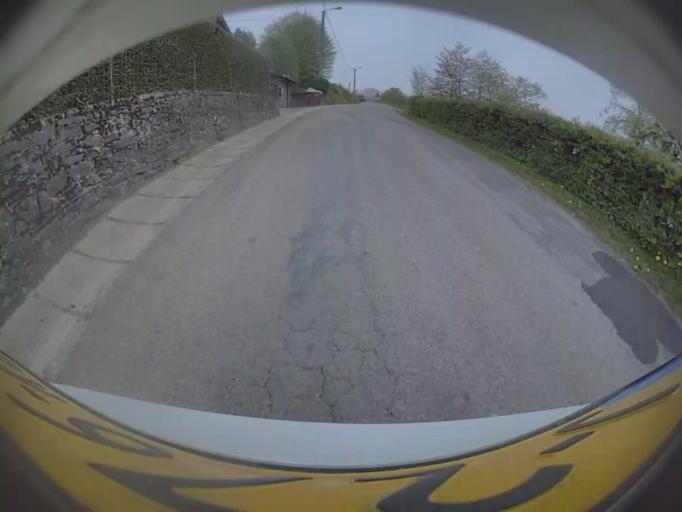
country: BE
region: Wallonia
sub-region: Province du Luxembourg
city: La Roche-en-Ardenne
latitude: 50.2341
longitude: 5.6203
